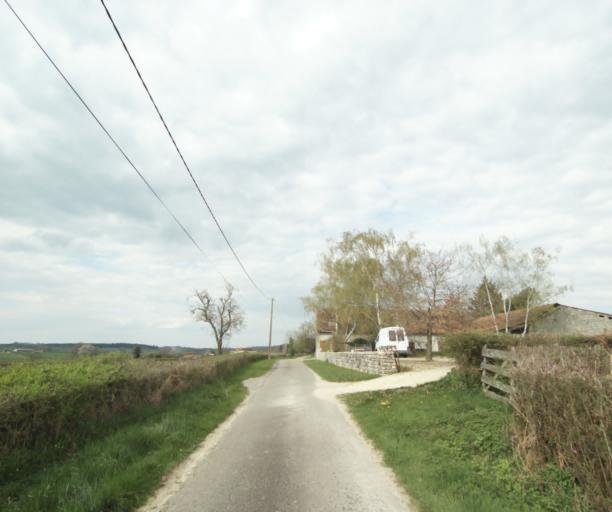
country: FR
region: Bourgogne
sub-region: Departement de Saone-et-Loire
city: Saint-Vallier
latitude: 46.5436
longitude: 4.4002
